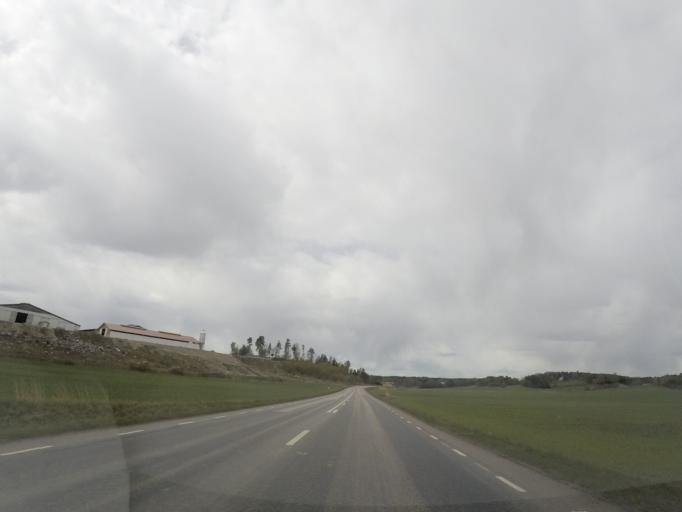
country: SE
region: Soedermanland
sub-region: Nykopings Kommun
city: Olstorp
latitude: 58.7457
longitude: 16.6517
